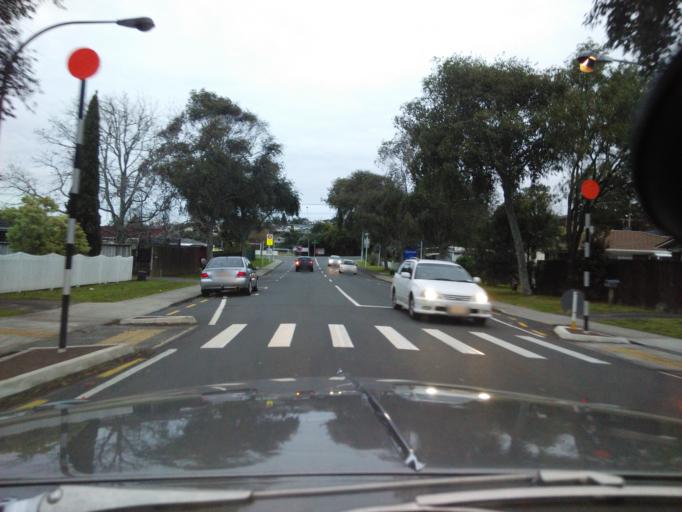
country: NZ
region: Auckland
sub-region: Auckland
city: North Shore
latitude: -36.7845
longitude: 174.7327
